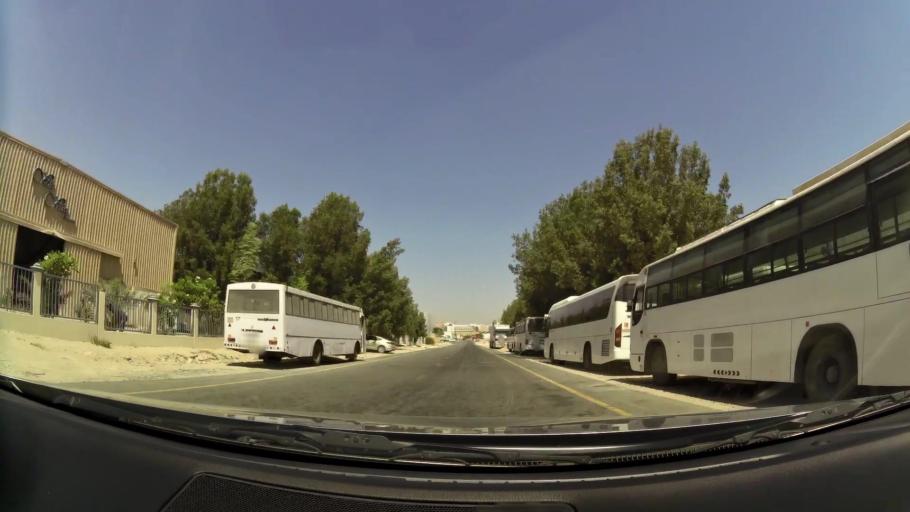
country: AE
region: Dubai
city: Dubai
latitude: 24.9867
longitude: 55.2119
